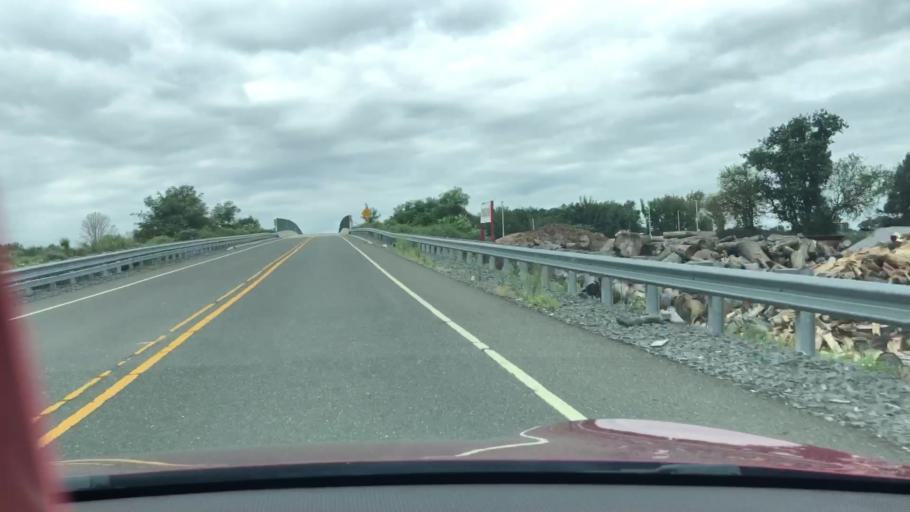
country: US
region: New Jersey
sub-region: Monmouth County
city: Allentown
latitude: 40.1894
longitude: -74.6037
